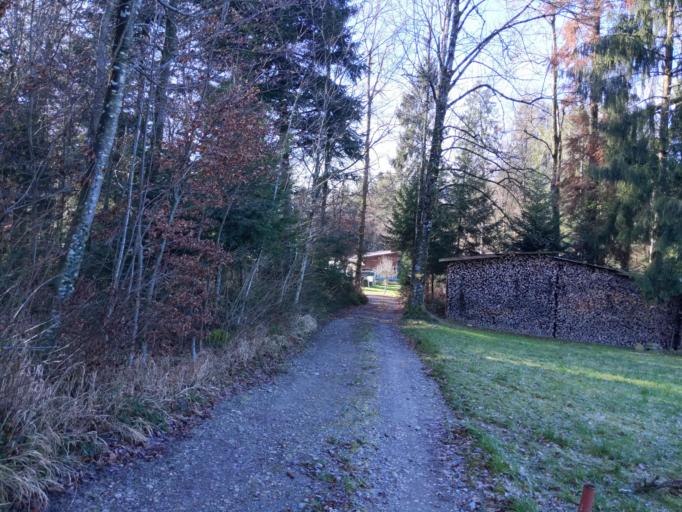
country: CH
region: Saint Gallen
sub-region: Wahlkreis See-Gaster
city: Eschenbach
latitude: 47.2320
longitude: 8.9312
